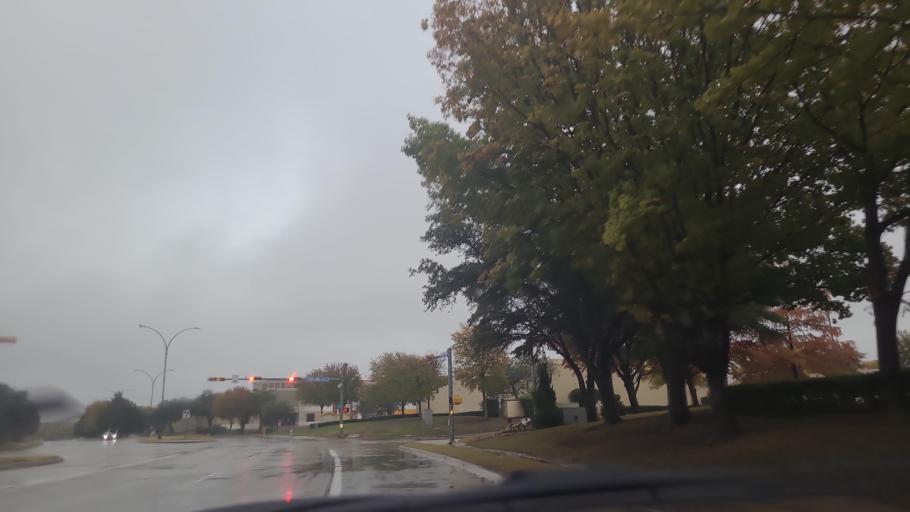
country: US
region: Texas
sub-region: Tarrant County
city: Dalworthington Gardens
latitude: 32.6822
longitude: -97.1270
